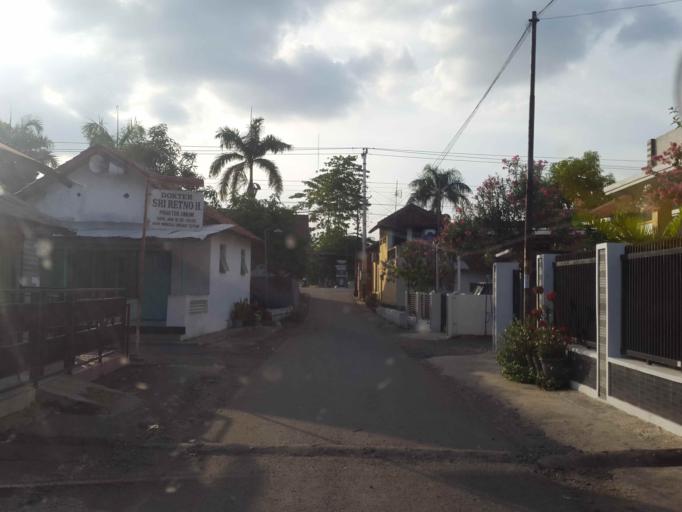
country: ID
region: Central Java
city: Slawi
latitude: -7.0052
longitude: 109.1414
